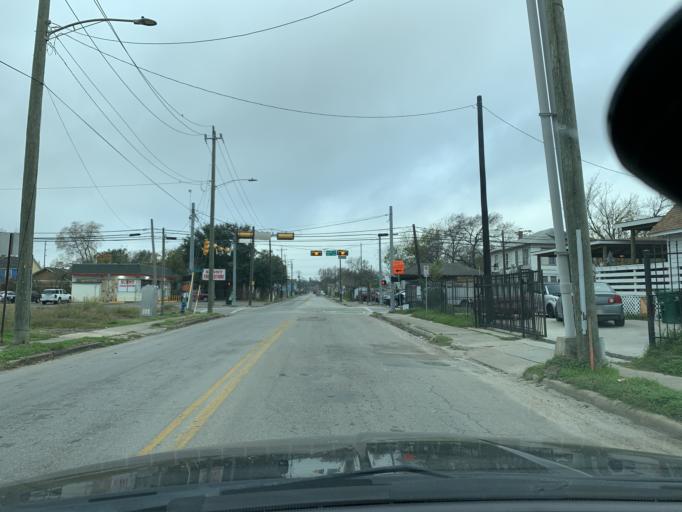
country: US
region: Texas
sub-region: Harris County
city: Houston
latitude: 29.7834
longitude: -95.3509
